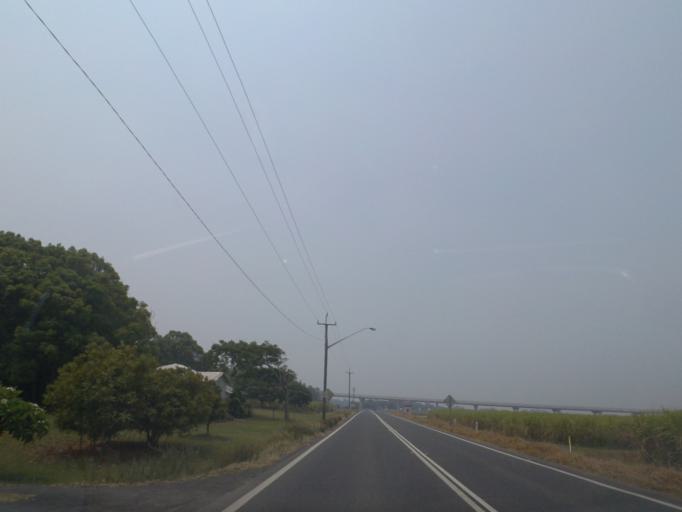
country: AU
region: New South Wales
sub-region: Richmond Valley
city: Evans Head
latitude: -29.0015
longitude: 153.4377
